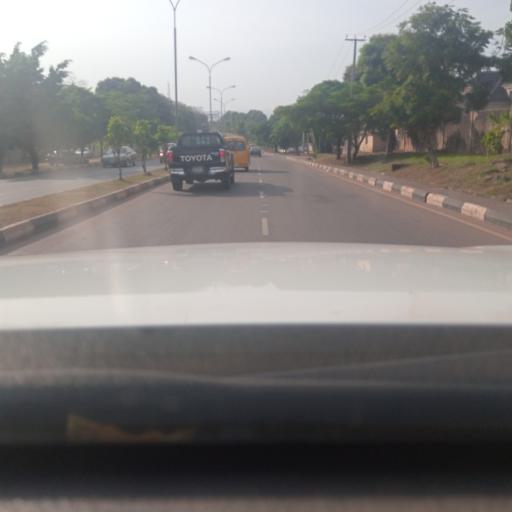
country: NG
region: Enugu
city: Enugu
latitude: 6.4399
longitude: 7.5163
